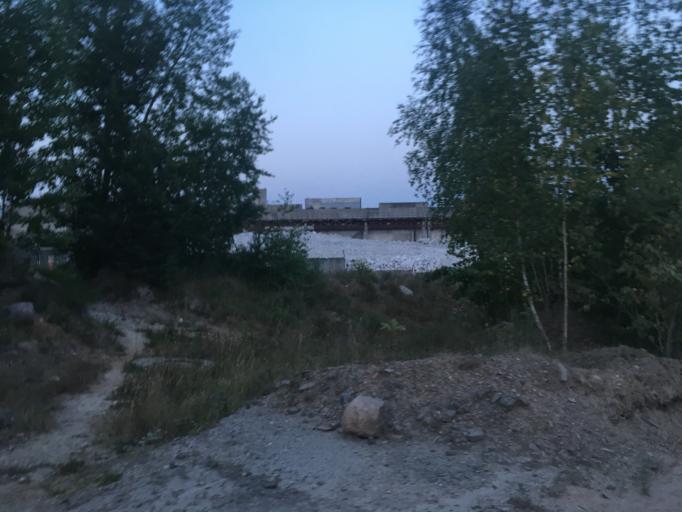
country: BY
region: Grodnenskaya
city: Hrodna
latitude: 53.7196
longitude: 23.7991
